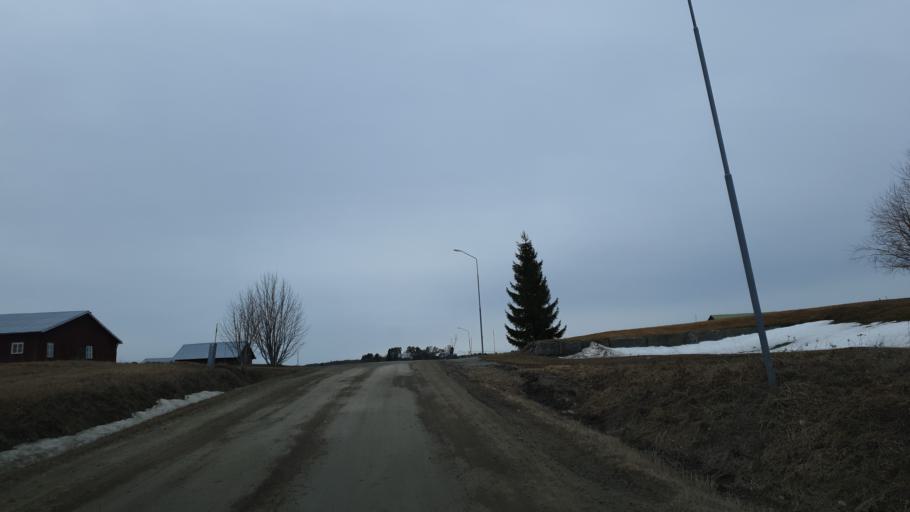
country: SE
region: Vaesterbotten
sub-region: Robertsfors Kommun
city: Robertsfors
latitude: 64.3809
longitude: 20.9158
